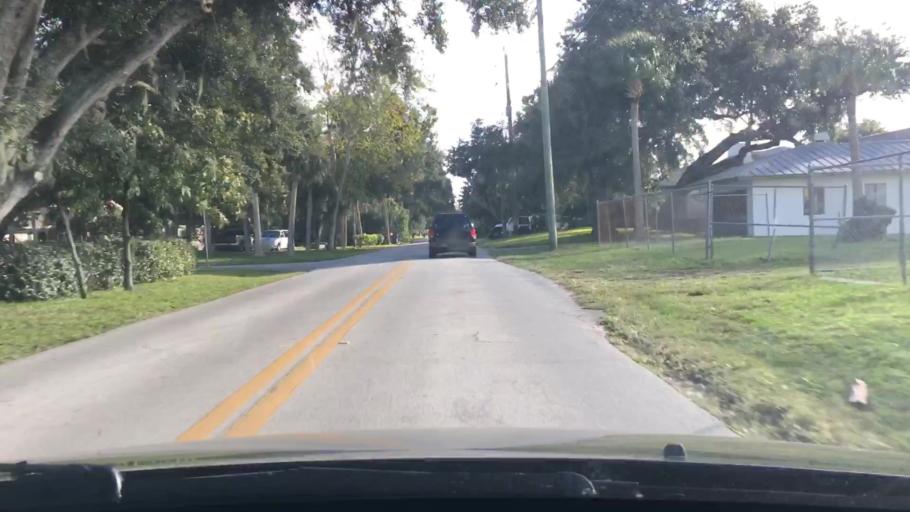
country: US
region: Florida
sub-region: Volusia County
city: Ormond-by-the-Sea
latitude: 29.3299
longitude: -81.0659
